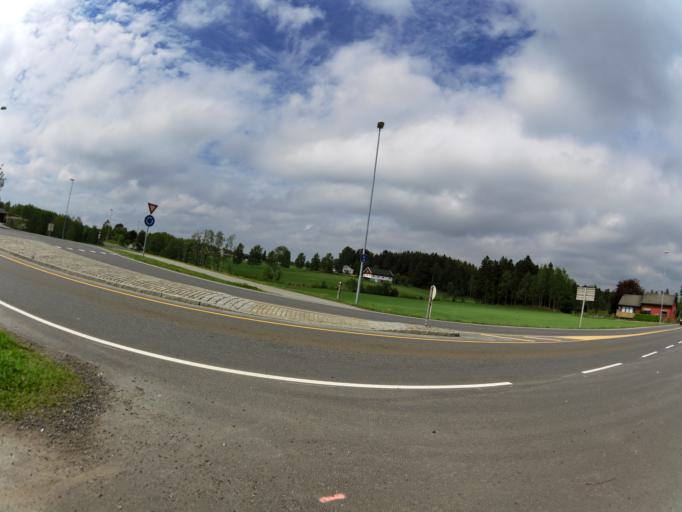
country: NO
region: Ostfold
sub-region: Rade
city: Karlshus
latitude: 59.3452
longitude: 10.9315
